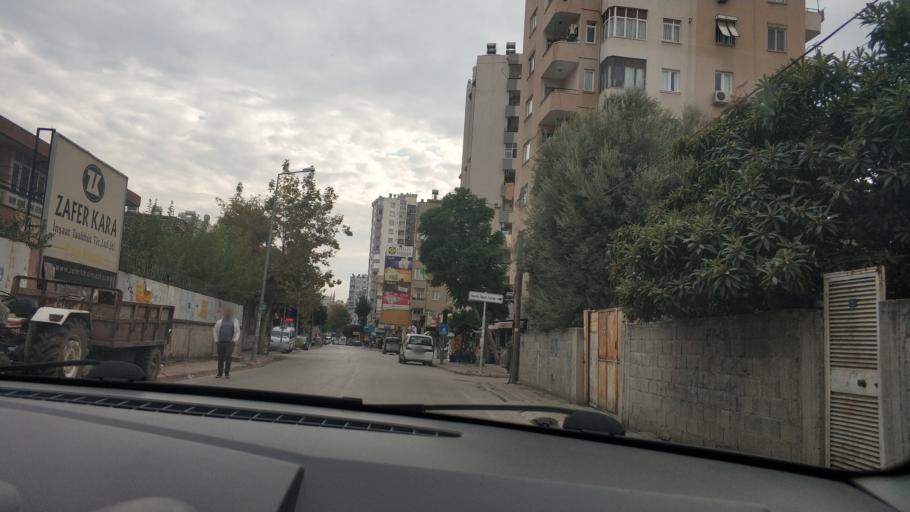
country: TR
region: Adana
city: Adana
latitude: 37.0090
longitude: 35.3154
